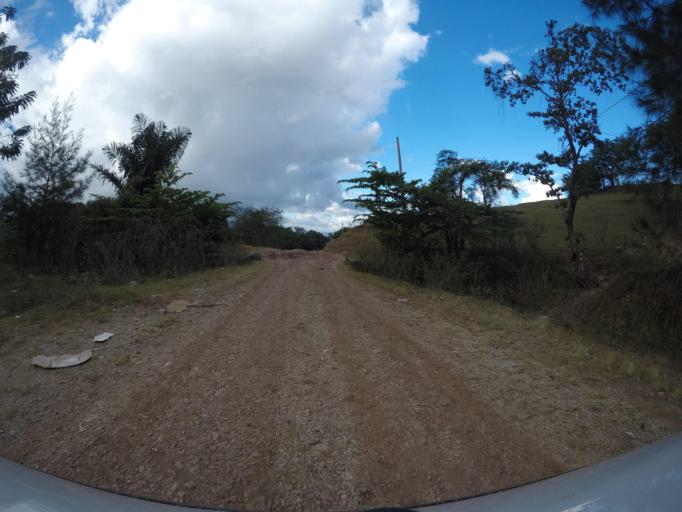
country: TL
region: Baucau
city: Venilale
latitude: -8.6875
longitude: 126.6617
